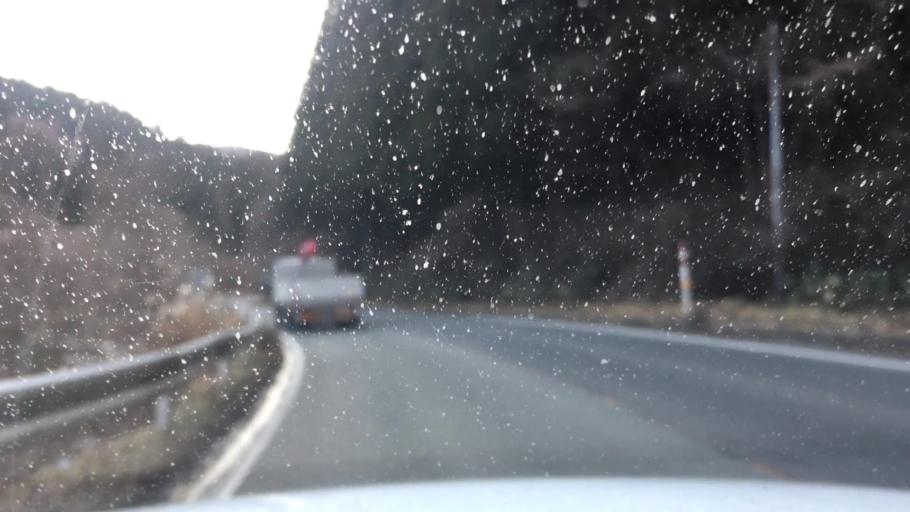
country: JP
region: Iwate
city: Morioka-shi
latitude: 39.6753
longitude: 141.2016
